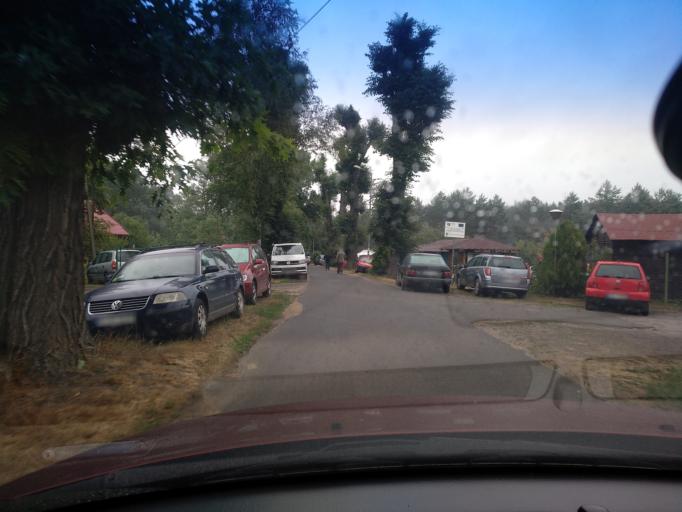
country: PL
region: Lower Silesian Voivodeship
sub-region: Powiat zgorzelecki
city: Wegliniec
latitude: 51.2640
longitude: 15.1959
